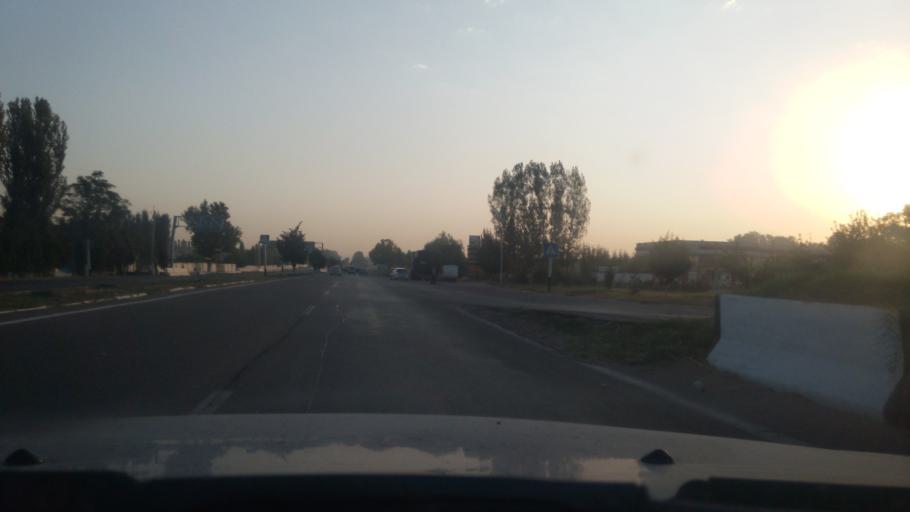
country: UZ
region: Toshkent
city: Yangiyul
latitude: 41.1645
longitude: 69.0567
